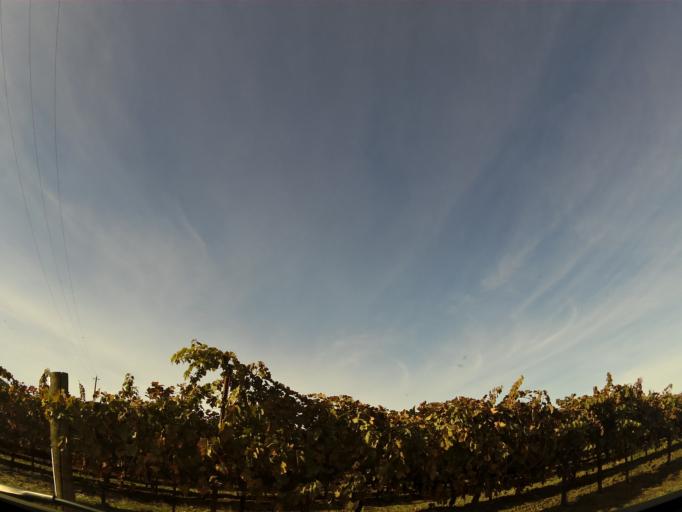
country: US
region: California
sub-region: San Benito County
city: Ridgemark
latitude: 36.7200
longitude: -121.3580
